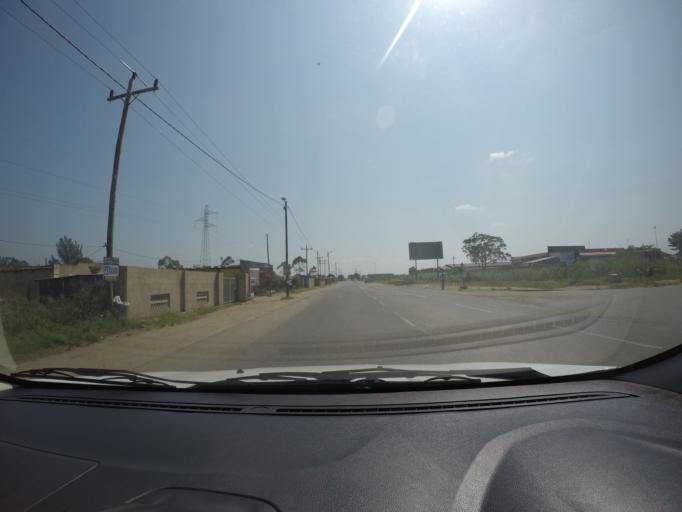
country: ZA
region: KwaZulu-Natal
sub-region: uThungulu District Municipality
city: eSikhawini
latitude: -28.8680
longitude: 31.9055
